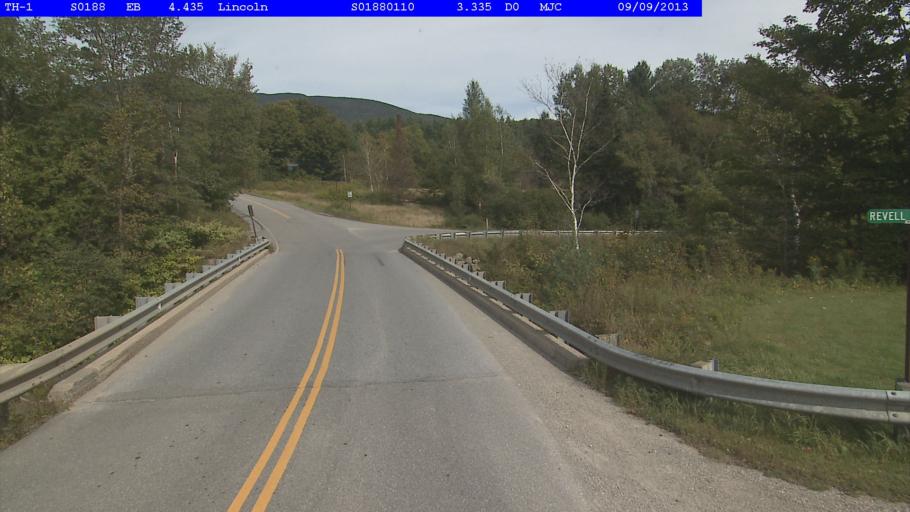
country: US
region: Vermont
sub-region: Addison County
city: Bristol
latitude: 44.0951
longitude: -72.9829
